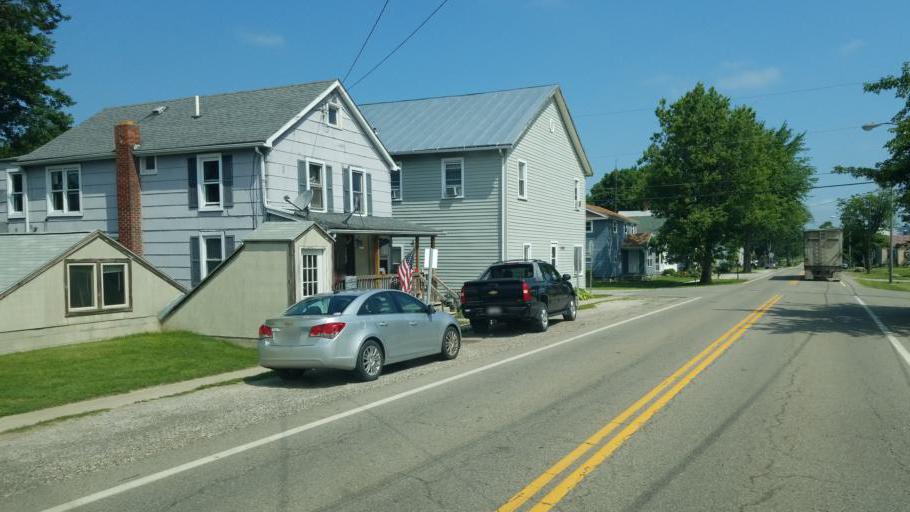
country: US
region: Ohio
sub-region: Crawford County
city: Galion
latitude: 40.7930
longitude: -82.8571
